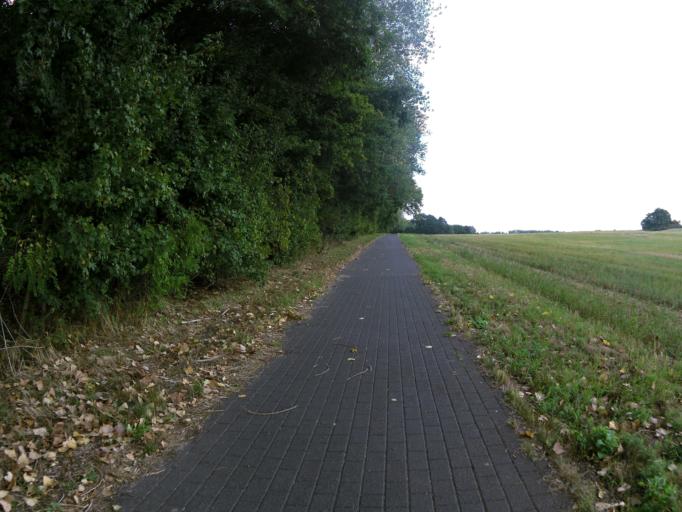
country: DE
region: Mecklenburg-Vorpommern
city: Seebad Bansin
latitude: 53.9436
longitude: 14.0927
